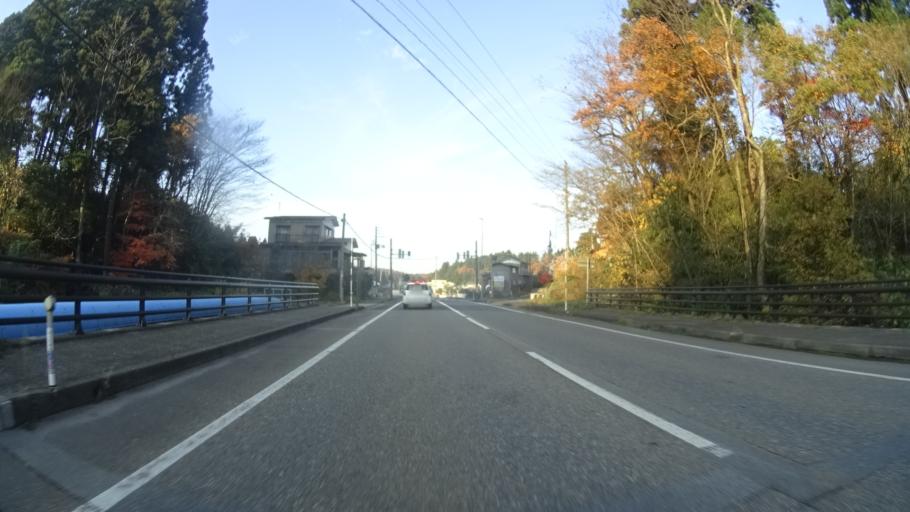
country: JP
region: Niigata
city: Nagaoka
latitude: 37.4286
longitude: 138.7266
